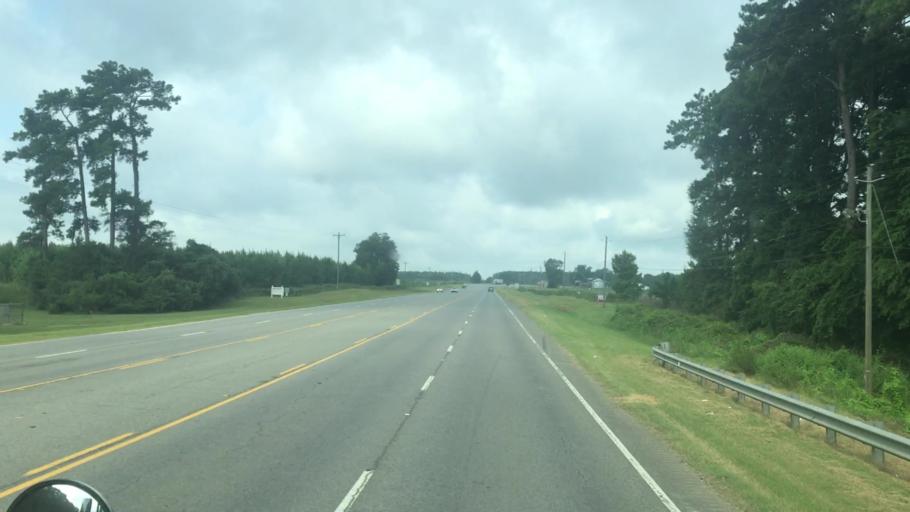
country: US
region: Georgia
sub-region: Miller County
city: Colquitt
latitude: 31.1705
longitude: -84.7450
